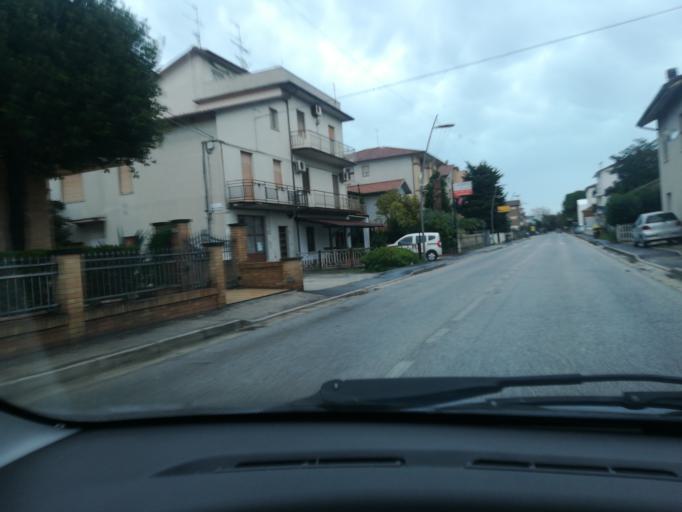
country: IT
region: The Marches
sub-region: Provincia di Macerata
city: Trodica
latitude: 43.2750
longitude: 13.5957
